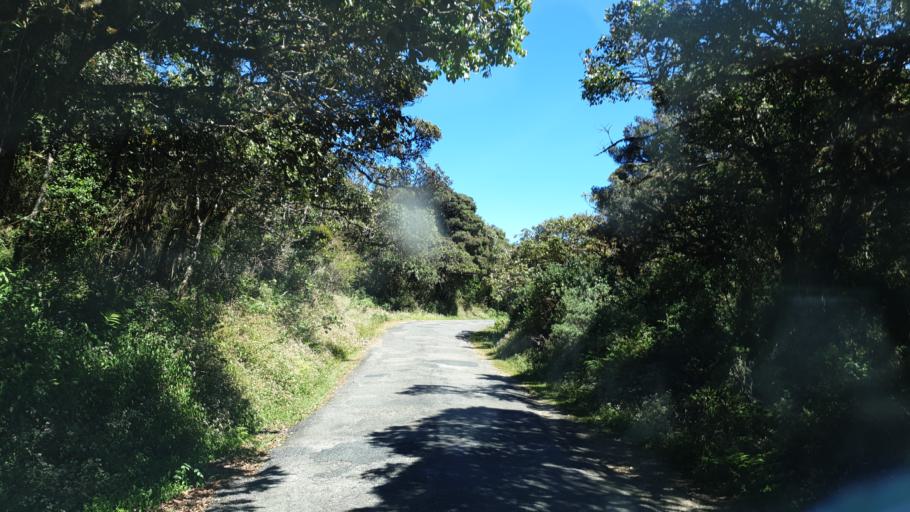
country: LK
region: Central
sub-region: Nuwara Eliya District
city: Nuwara Eliya
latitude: 6.8292
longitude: 80.8057
